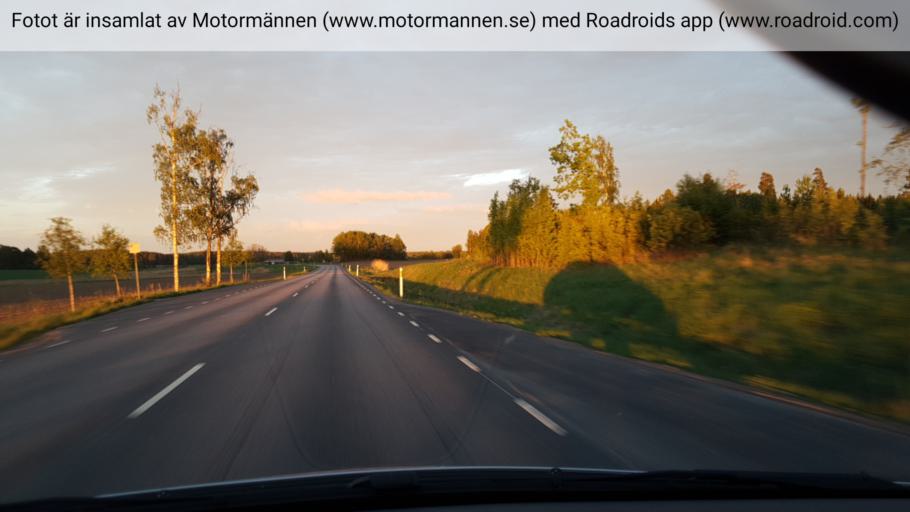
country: SE
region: Vaestmanland
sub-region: Hallstahammars Kommun
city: Kolback
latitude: 59.5599
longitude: 16.3249
